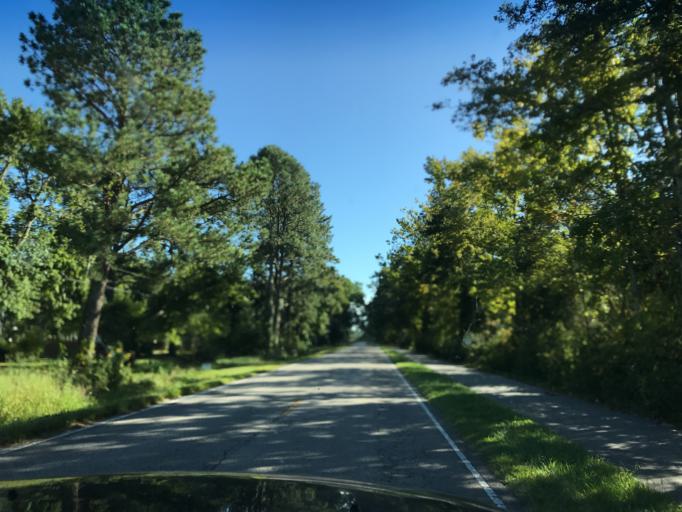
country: US
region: Virginia
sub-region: City of Portsmouth
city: Portsmouth Heights
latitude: 36.7013
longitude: -76.3559
